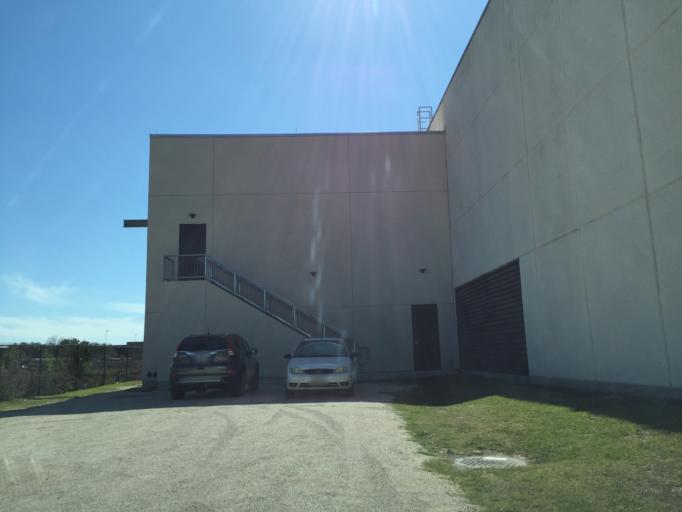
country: US
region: Texas
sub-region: Travis County
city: Wells Branch
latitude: 30.3973
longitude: -97.7248
